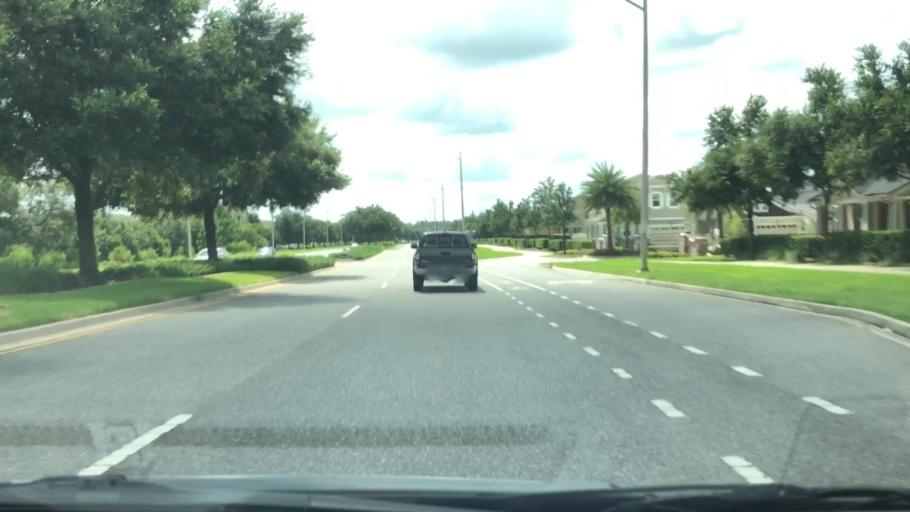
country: US
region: Florida
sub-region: Saint Johns County
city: Fruit Cove
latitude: 30.1164
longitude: -81.5212
